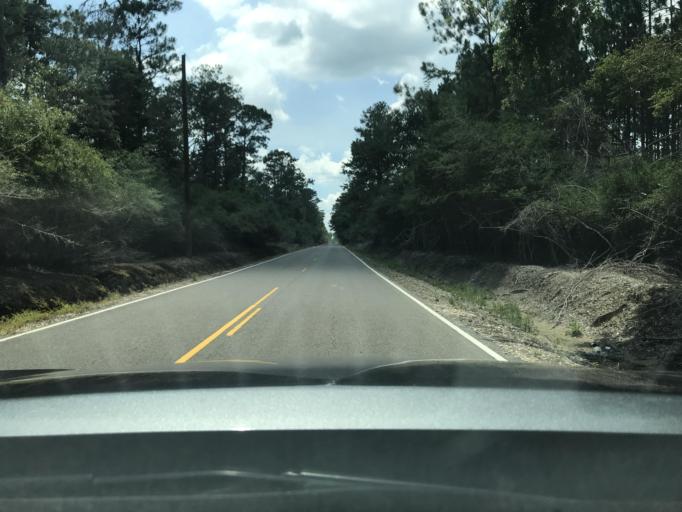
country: US
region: Louisiana
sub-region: Calcasieu Parish
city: Moss Bluff
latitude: 30.3298
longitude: -93.1333
